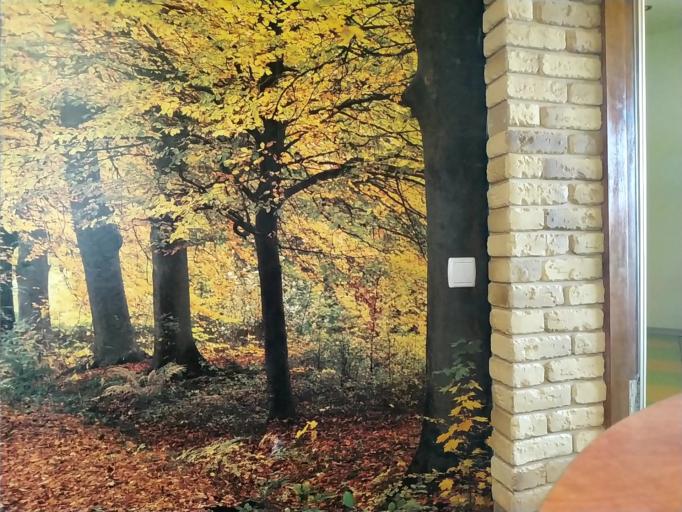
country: RU
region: Arkhangelskaya
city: Kargopol'
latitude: 60.8006
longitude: 38.8893
